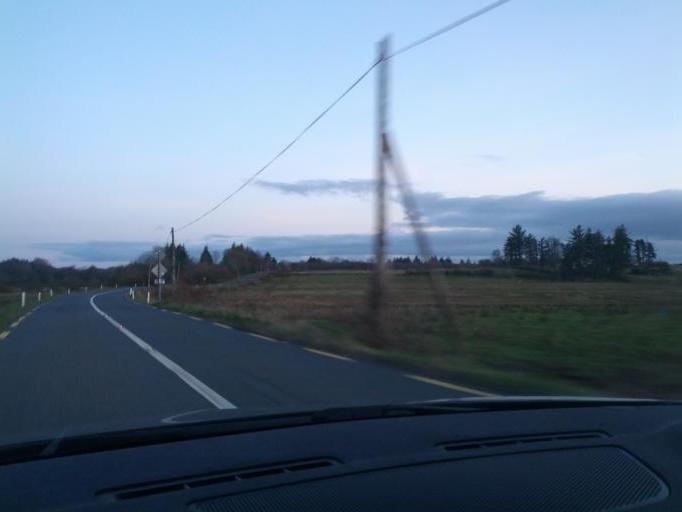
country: IE
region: Connaught
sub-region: Roscommon
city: Boyle
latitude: 53.8972
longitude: -8.2522
